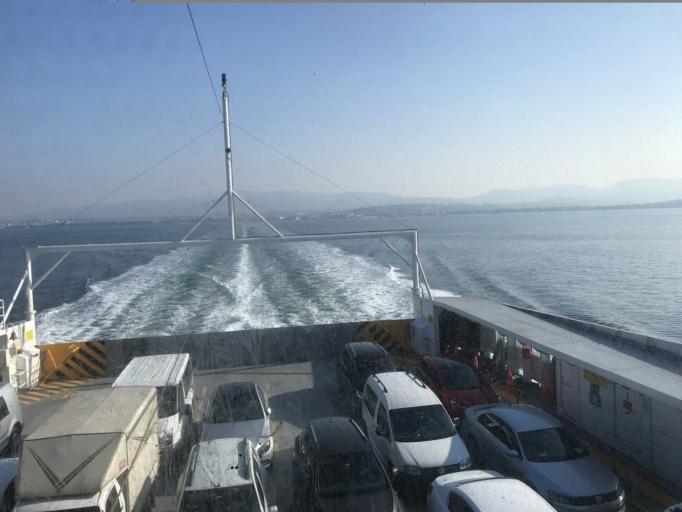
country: TR
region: Yalova
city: Yalova
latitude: 40.6859
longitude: 29.2602
